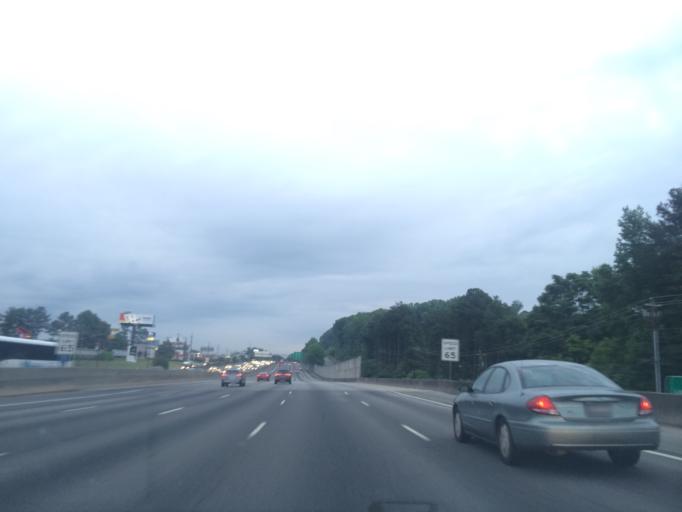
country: US
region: Georgia
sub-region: DeKalb County
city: North Druid Hills
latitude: 33.8352
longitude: -84.3281
